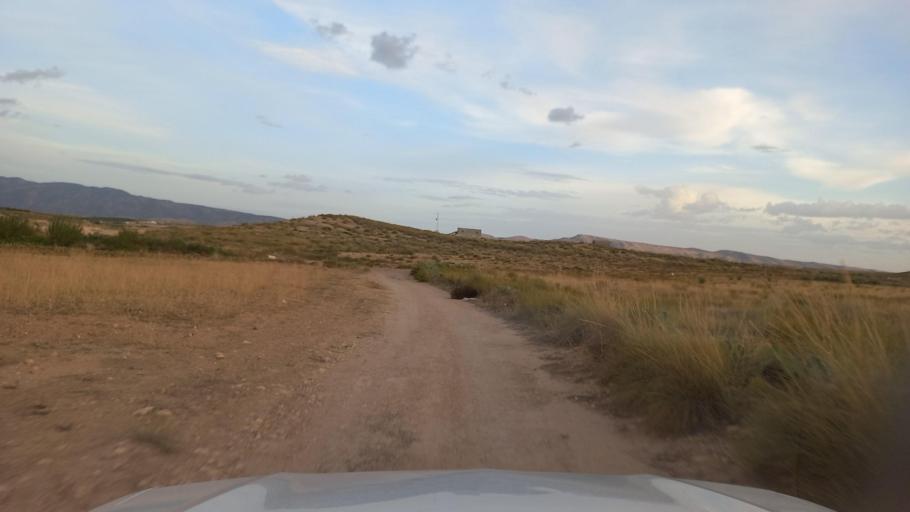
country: TN
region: Al Qasrayn
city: Sbiba
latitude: 35.4094
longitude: 9.0875
